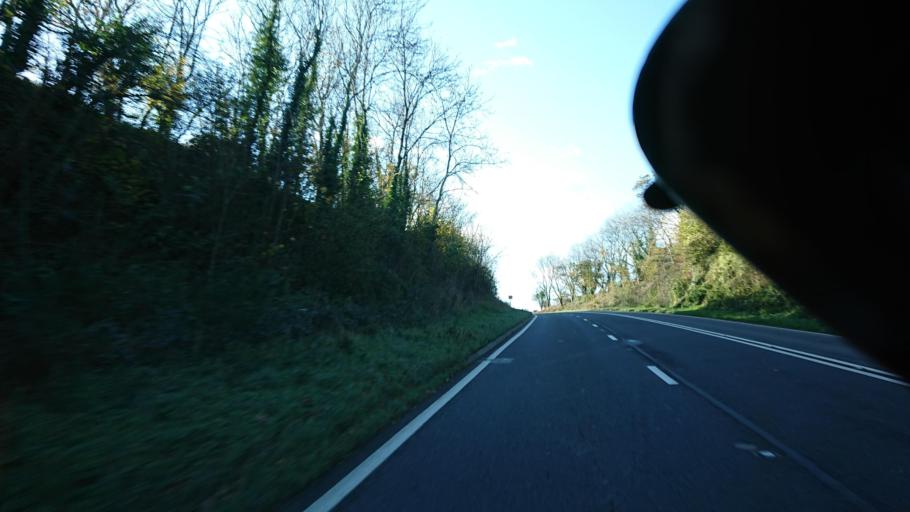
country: GB
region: England
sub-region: Cornwall
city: Pillaton
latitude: 50.4118
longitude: -4.3363
